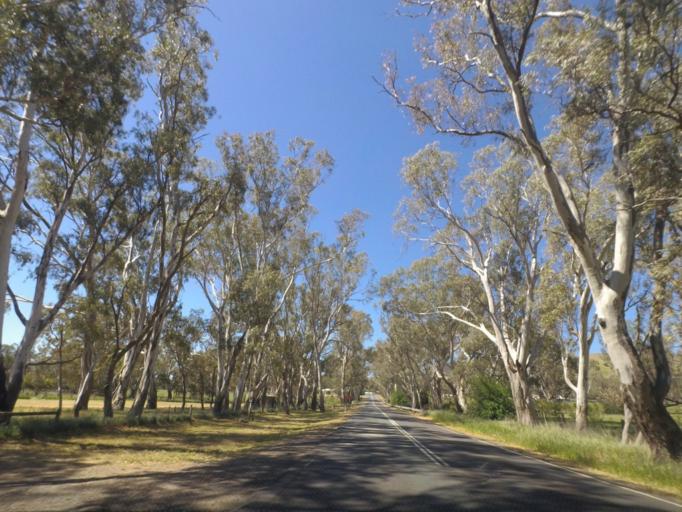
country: AU
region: Victoria
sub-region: Hume
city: Sunbury
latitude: -37.0488
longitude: 144.7951
